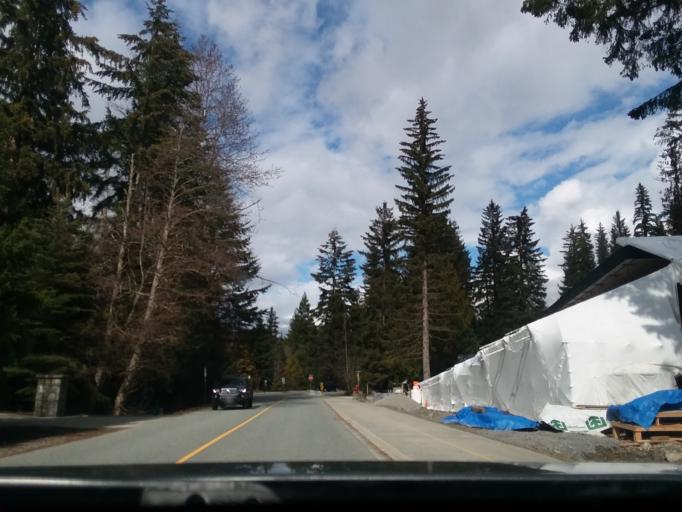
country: CA
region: British Columbia
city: Whistler
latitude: 50.1255
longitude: -122.9694
